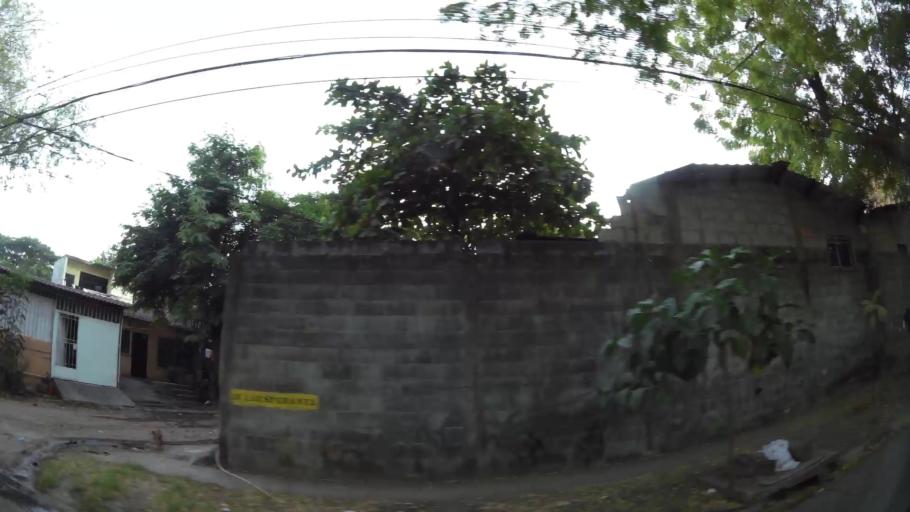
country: SV
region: San Miguel
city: San Miguel
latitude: 13.4819
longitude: -88.1586
